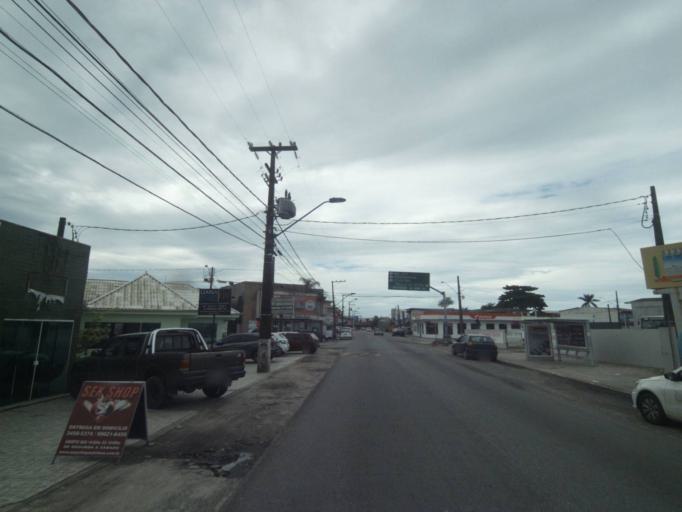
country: BR
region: Parana
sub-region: Guaratuba
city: Guaratuba
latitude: -25.8190
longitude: -48.5393
